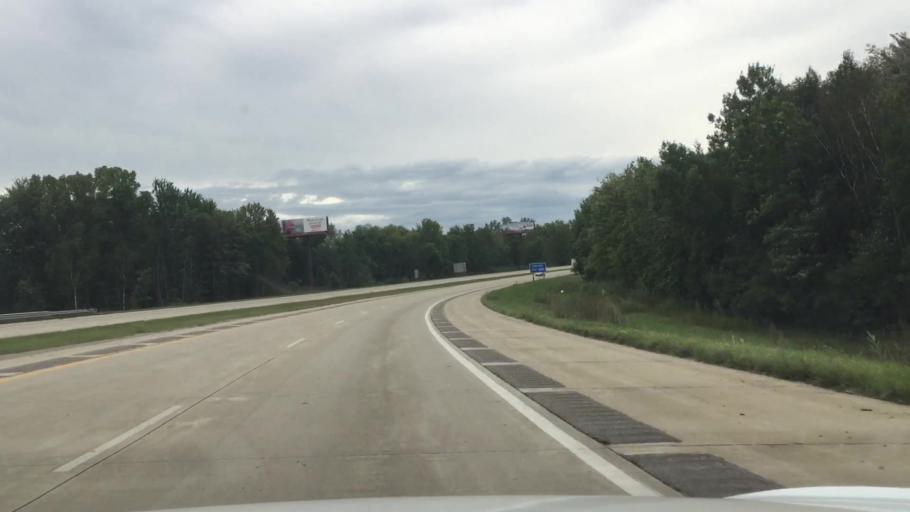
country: US
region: Michigan
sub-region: Saint Clair County
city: Marysville
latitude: 42.9600
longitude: -82.4899
